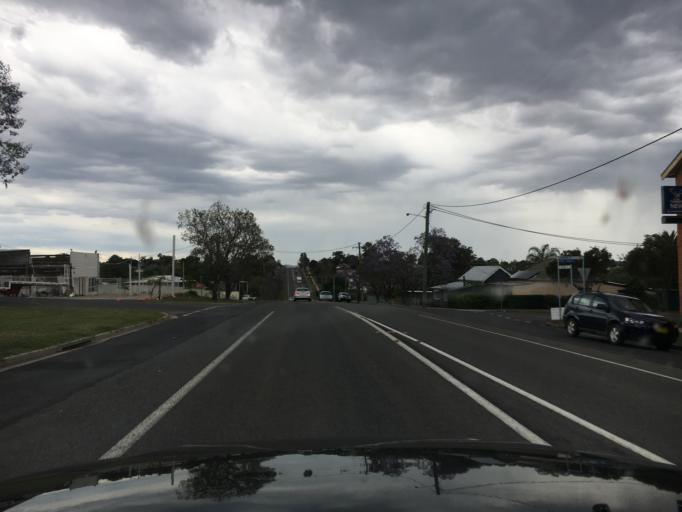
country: AU
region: New South Wales
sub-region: Muswellbrook
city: Muswellbrook
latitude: -32.1675
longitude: 150.8915
